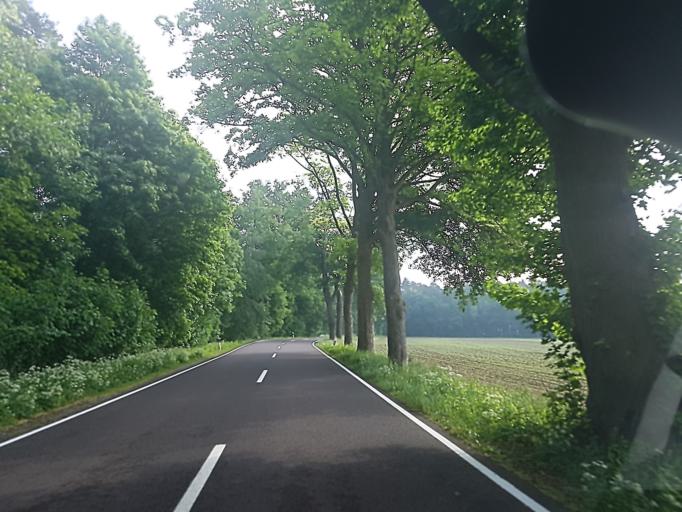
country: DE
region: Saxony-Anhalt
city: Lindau
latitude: 52.0457
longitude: 12.2595
